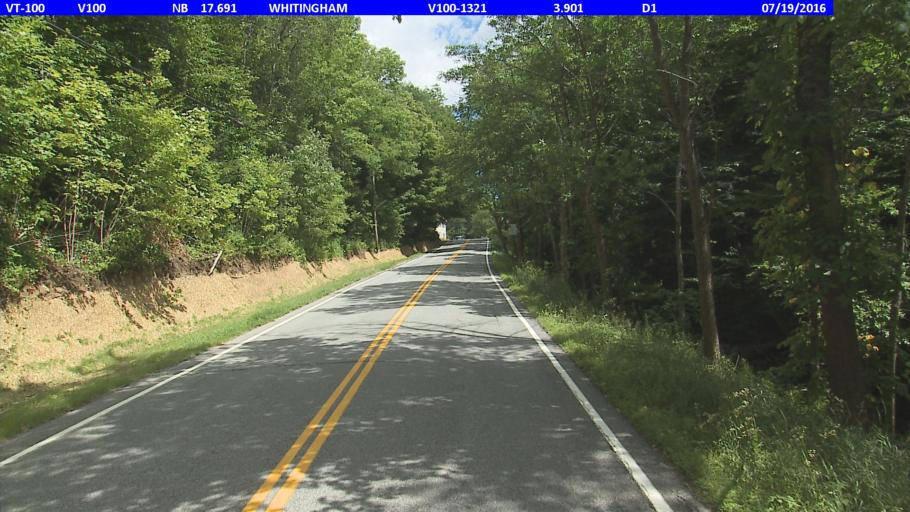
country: US
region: Massachusetts
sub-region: Franklin County
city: Charlemont
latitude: 42.7899
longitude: -72.8869
